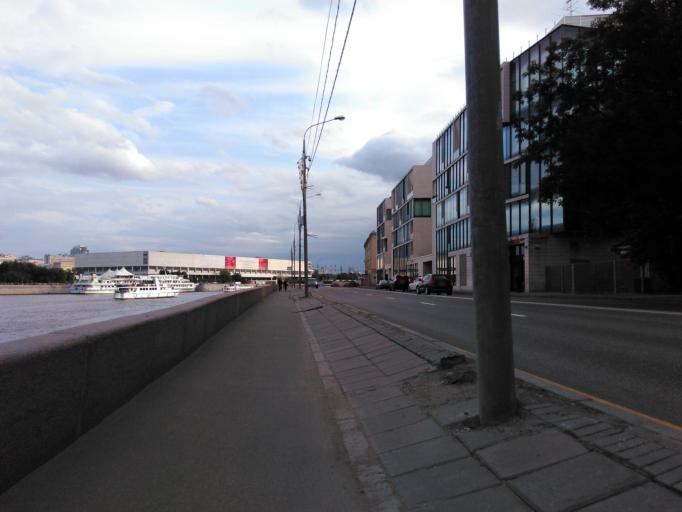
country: RU
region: Moscow
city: Moscow
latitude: 55.7406
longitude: 37.6065
